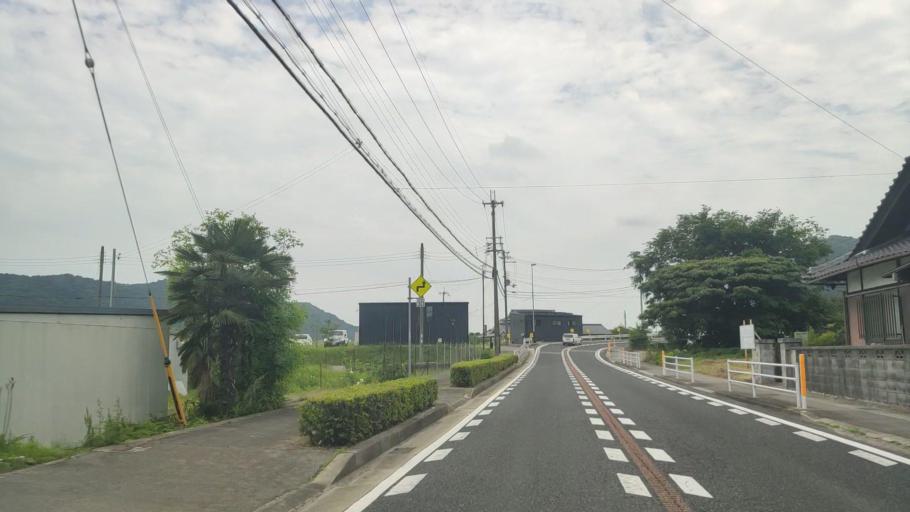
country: JP
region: Hyogo
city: Tatsunocho-tominaga
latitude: 34.8849
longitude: 134.5470
